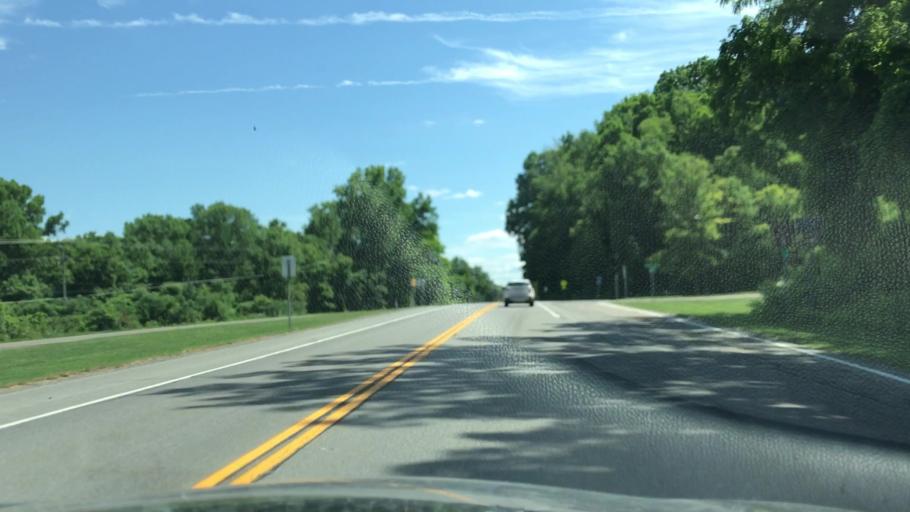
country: US
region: New York
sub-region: Livingston County
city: Mount Morris
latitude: 42.7424
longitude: -77.8829
